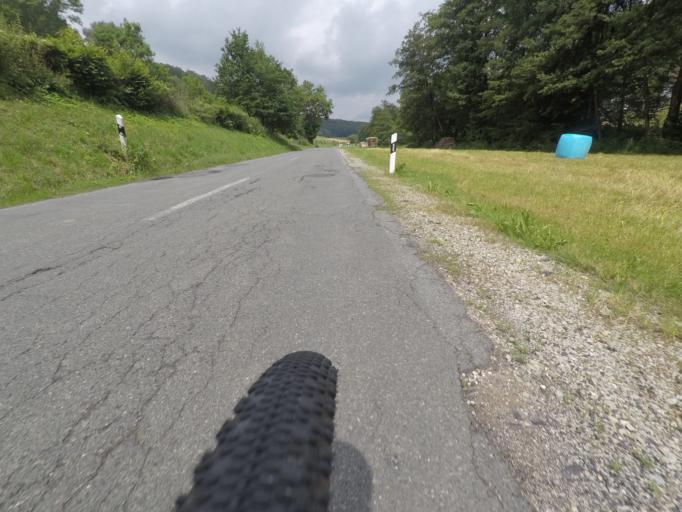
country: DE
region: Hesse
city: Waldkappel
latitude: 51.1798
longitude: 9.8161
